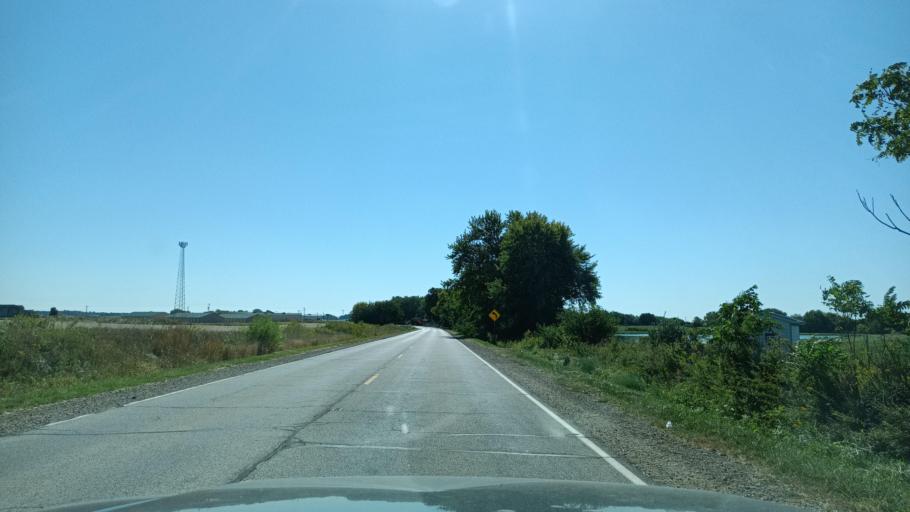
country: US
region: Illinois
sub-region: Peoria County
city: Elmwood
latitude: 40.8345
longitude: -89.8752
